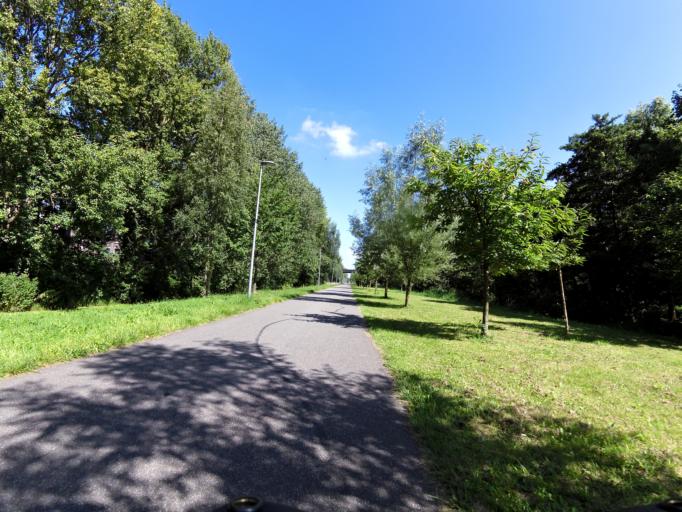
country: NL
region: South Holland
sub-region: Gemeente Rotterdam
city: Delfshaven
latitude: 51.8691
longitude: 4.4732
